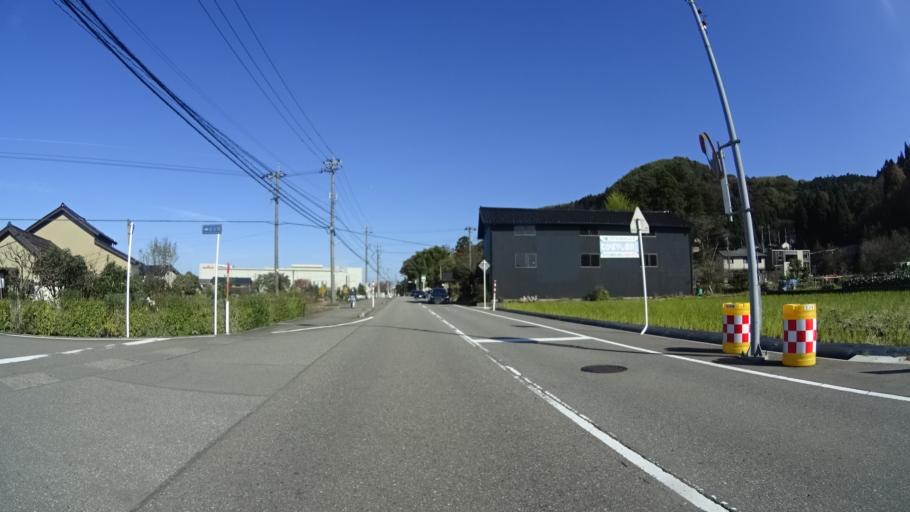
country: JP
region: Ishikawa
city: Tsurugi-asahimachi
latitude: 36.4893
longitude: 136.6186
